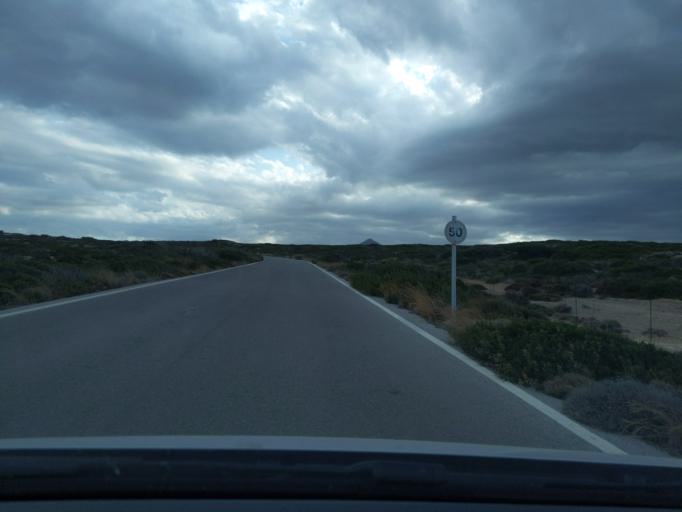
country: GR
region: Crete
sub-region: Nomos Lasithiou
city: Palekastro
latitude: 35.2448
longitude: 26.2491
